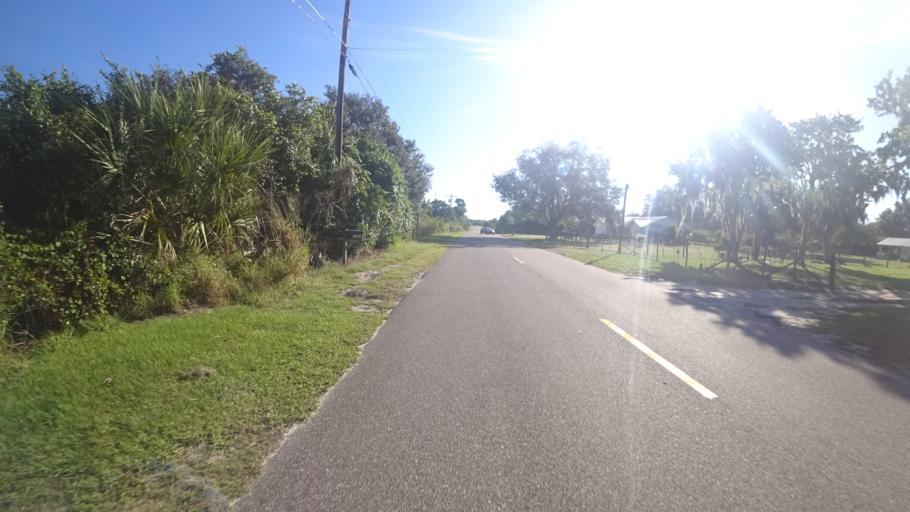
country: US
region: Florida
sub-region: Manatee County
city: Memphis
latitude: 27.5903
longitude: -82.5311
